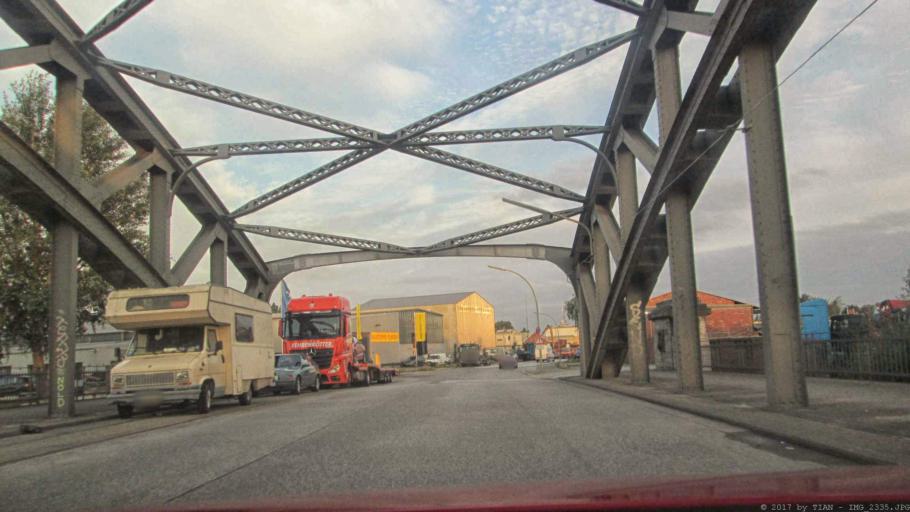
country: DE
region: Hamburg
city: Rothenburgsort
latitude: 53.5362
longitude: 10.0725
